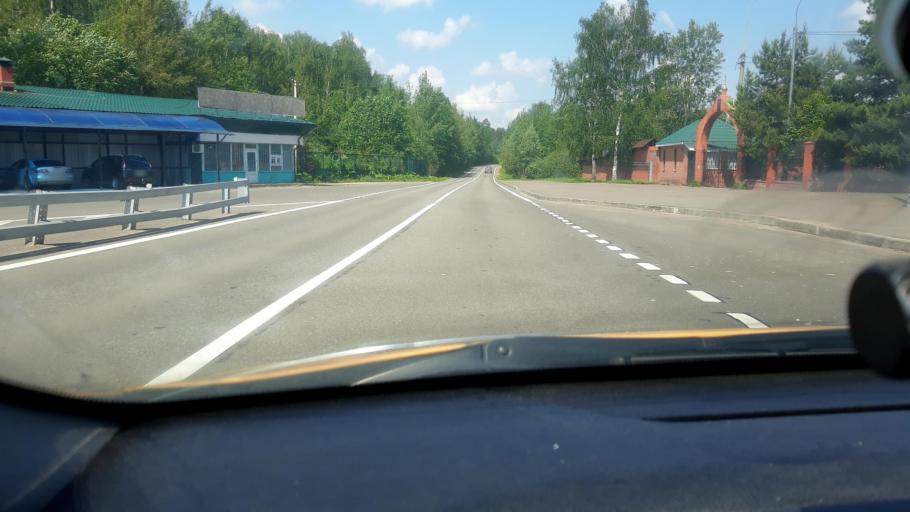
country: RU
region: Moskovskaya
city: Yakovlevskoye
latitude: 55.4535
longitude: 37.8928
